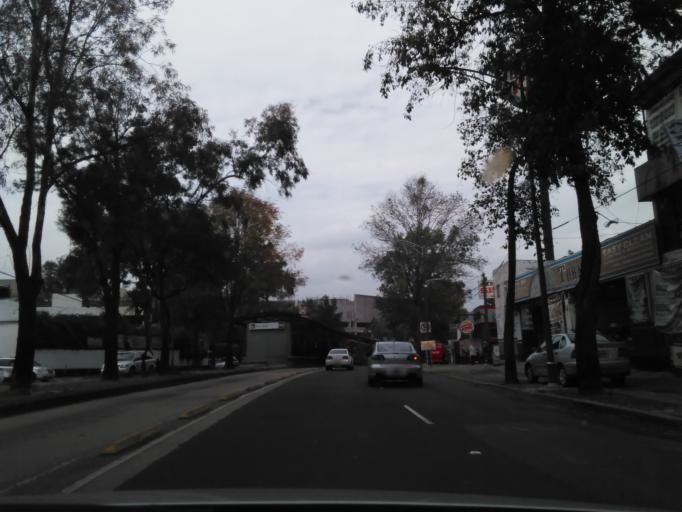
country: MX
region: Mexico City
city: Tlalpan
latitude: 19.2827
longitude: -99.1748
